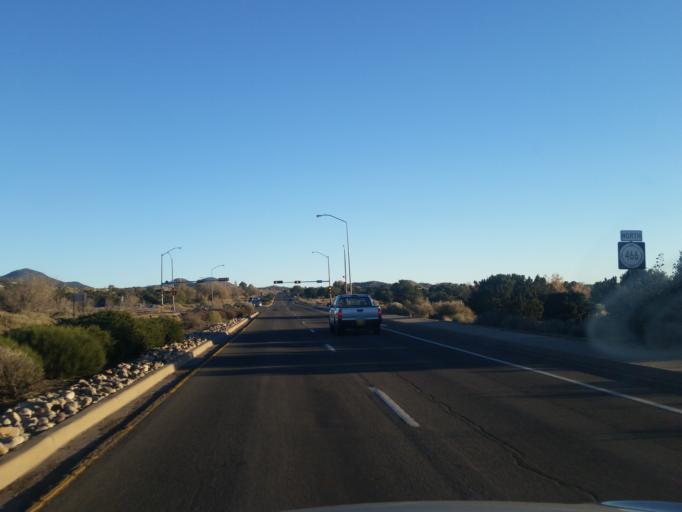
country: US
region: New Mexico
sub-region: Santa Fe County
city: Santa Fe
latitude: 35.6526
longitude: -105.9372
